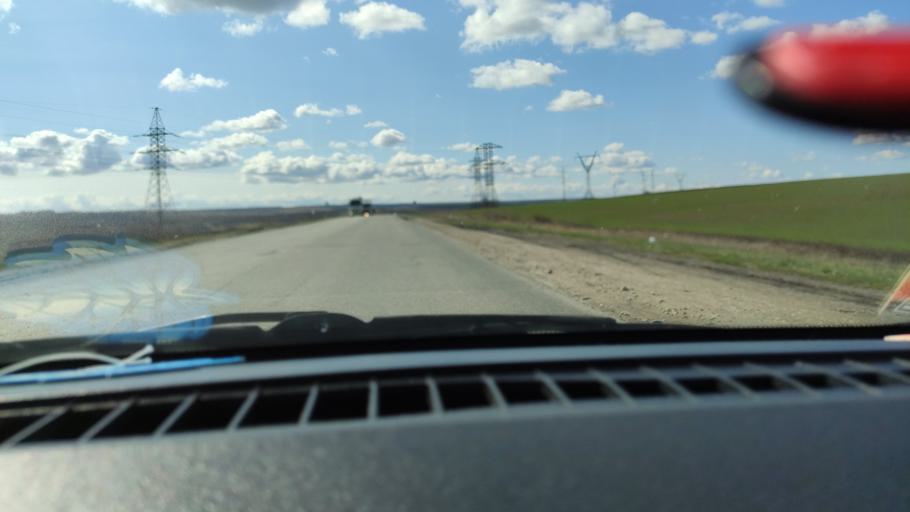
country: RU
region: Samara
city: Varlamovo
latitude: 53.0798
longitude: 48.3543
